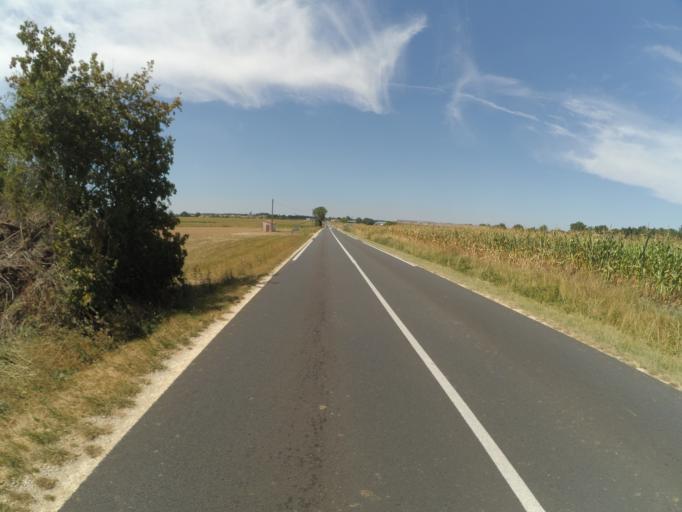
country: FR
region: Poitou-Charentes
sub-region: Departement de la Vienne
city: Saint-Maurice-la-Clouere
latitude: 46.3647
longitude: 0.4276
